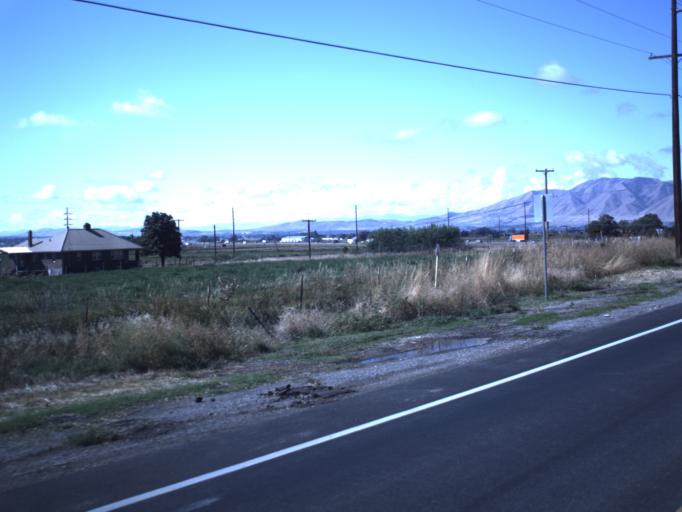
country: US
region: Utah
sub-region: Utah County
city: Spanish Fork
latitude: 40.0984
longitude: -111.6866
